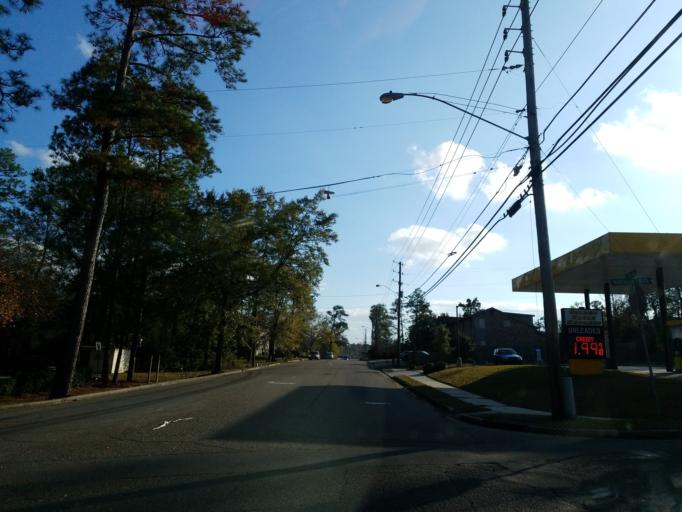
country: US
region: Mississippi
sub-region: Lamar County
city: Arnold Line
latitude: 31.3286
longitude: -89.3456
